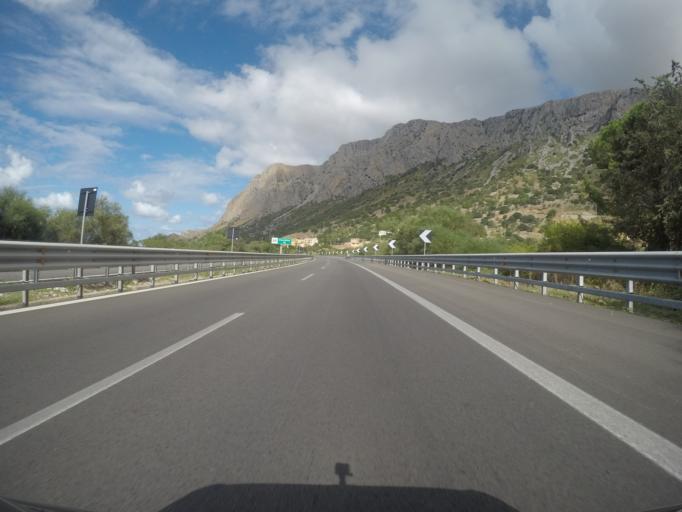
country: IT
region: Sicily
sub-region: Palermo
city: Cinisi
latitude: 38.1500
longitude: 13.1117
